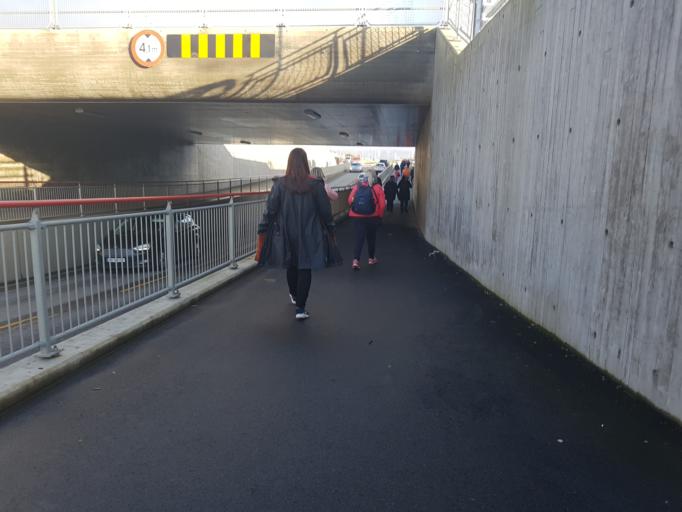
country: NO
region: Akershus
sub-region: Ullensaker
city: Jessheim
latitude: 60.1445
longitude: 11.1778
